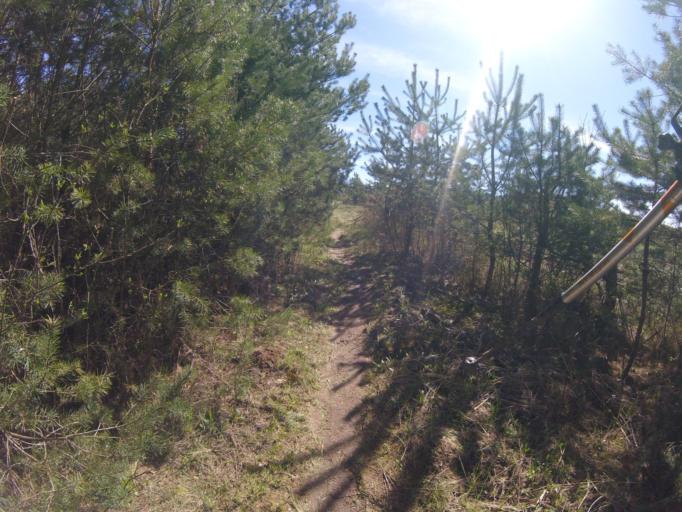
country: HU
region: Borsod-Abauj-Zemplen
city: Szendro
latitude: 48.4066
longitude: 20.7505
